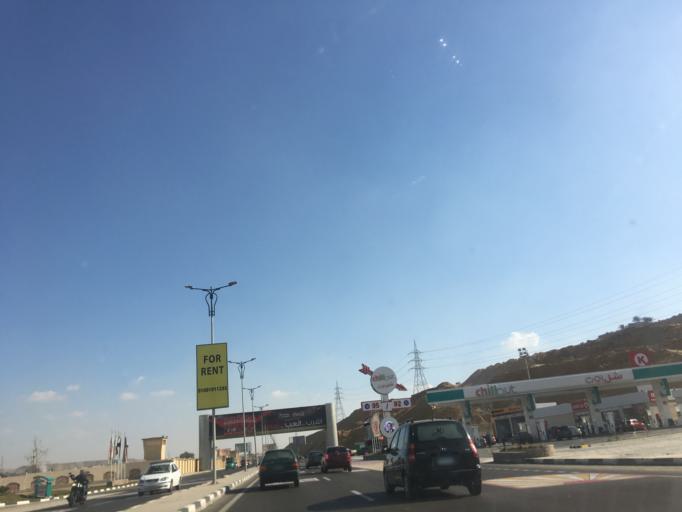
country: EG
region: Muhafazat al Qahirah
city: Cairo
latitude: 30.0219
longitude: 31.3287
